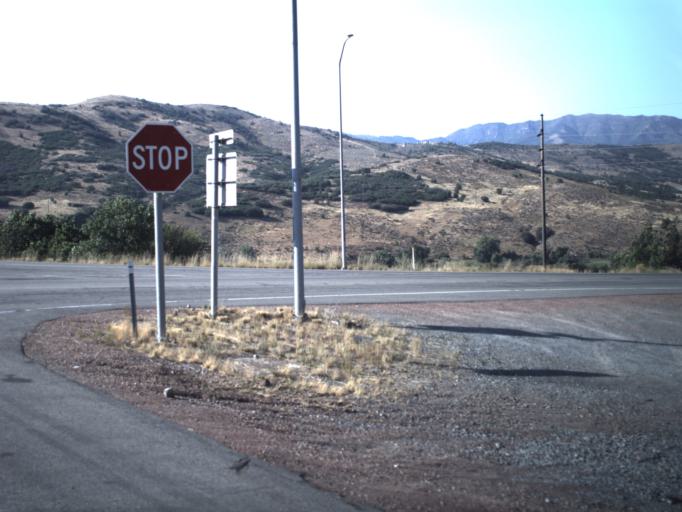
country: US
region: Utah
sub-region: Salt Lake County
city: Mount Olympus
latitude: 40.7521
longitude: -111.7127
